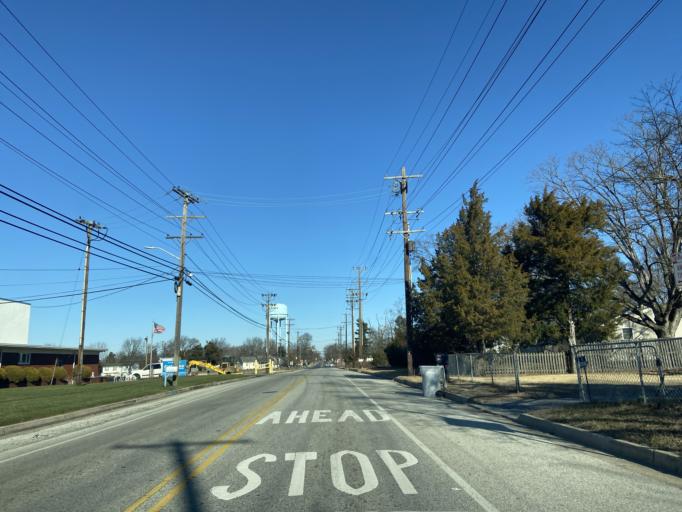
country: US
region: New Jersey
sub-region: Cumberland County
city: Vineland
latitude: 39.4931
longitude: -75.0610
